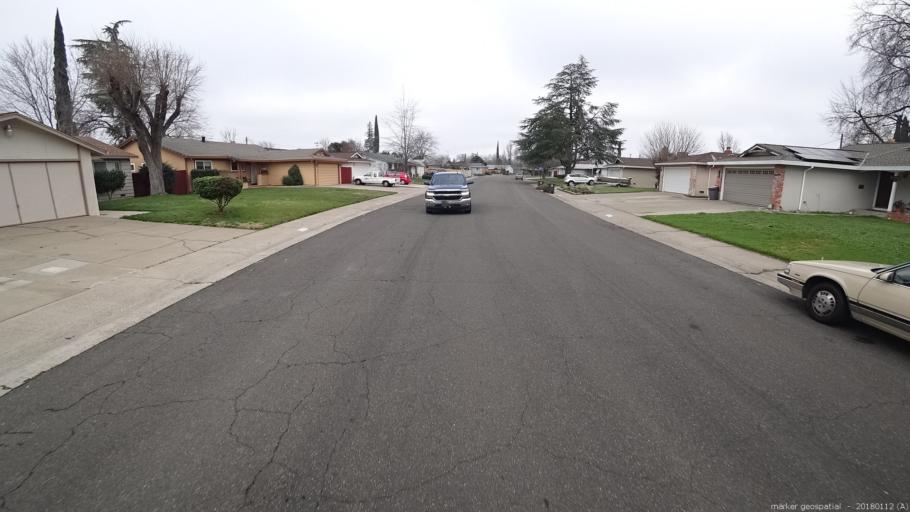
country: US
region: California
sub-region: Sacramento County
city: Rancho Cordova
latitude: 38.6081
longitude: -121.2889
